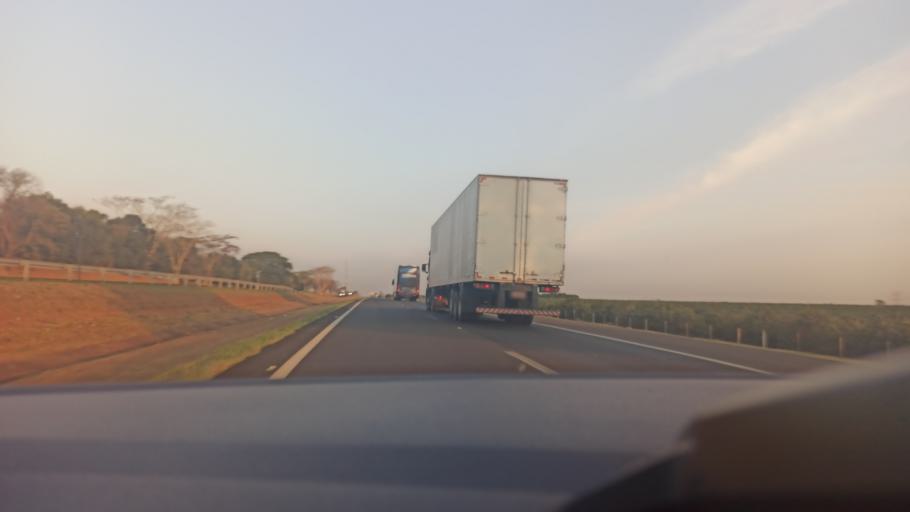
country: BR
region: Sao Paulo
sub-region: Santa Adelia
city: Santa Adelia
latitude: -21.4027
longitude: -48.7039
